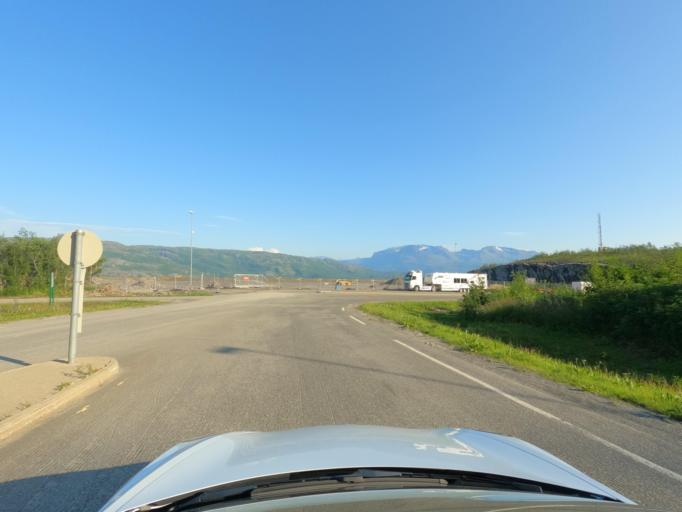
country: NO
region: Nordland
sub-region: Narvik
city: Bjerkvik
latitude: 68.5436
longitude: 17.4959
